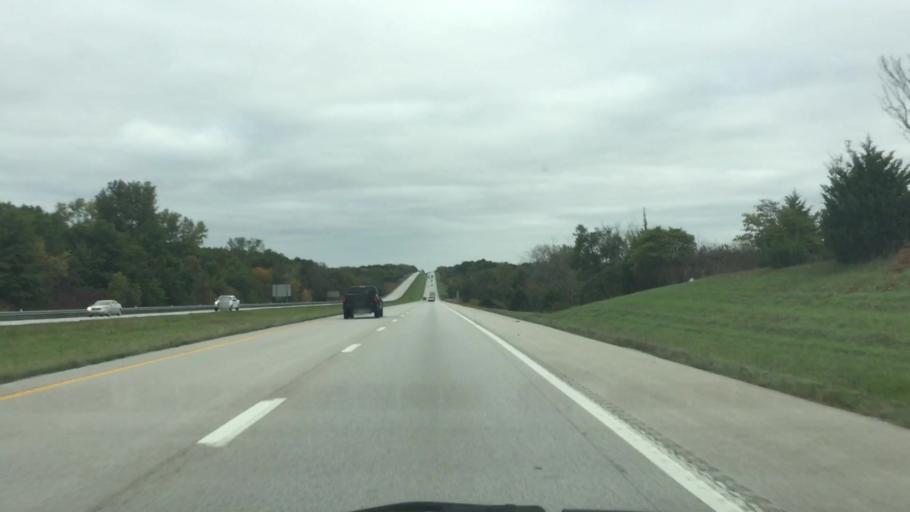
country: US
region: Missouri
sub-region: Clinton County
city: Cameron
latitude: 39.7657
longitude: -94.2156
